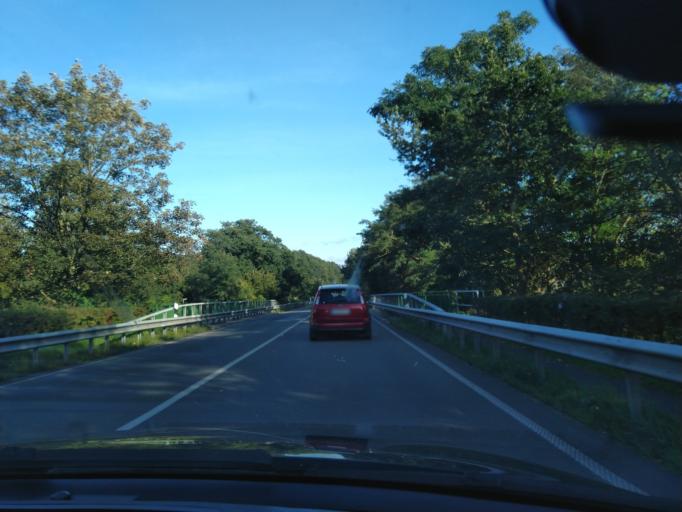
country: DE
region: Lower Saxony
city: Leer
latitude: 53.2385
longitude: 7.4672
